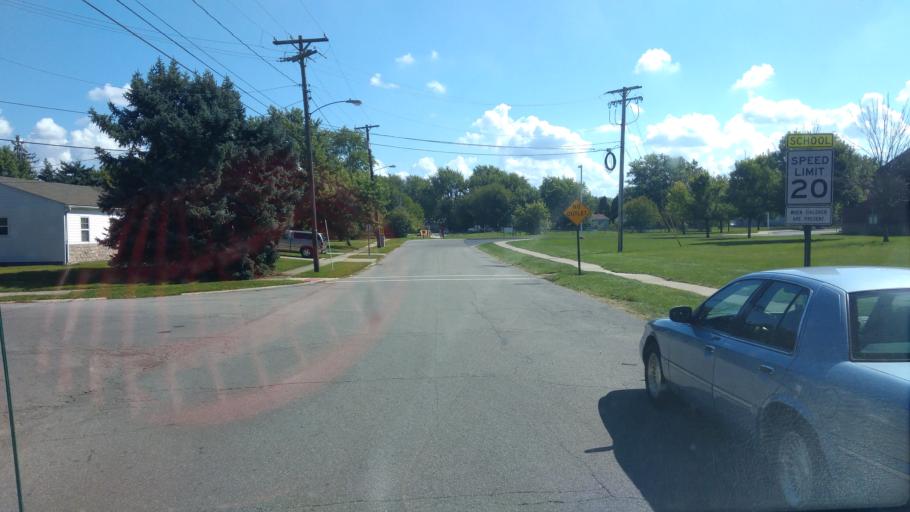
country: US
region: Ohio
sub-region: Marion County
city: Marion
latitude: 40.6089
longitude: -83.1179
